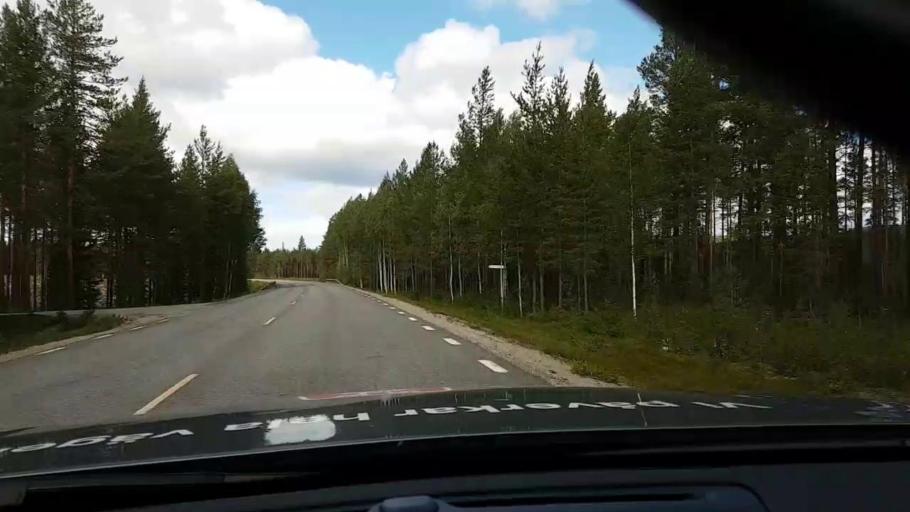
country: SE
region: Vaesternorrland
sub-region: OErnskoeldsviks Kommun
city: Bredbyn
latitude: 63.5365
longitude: 17.9649
